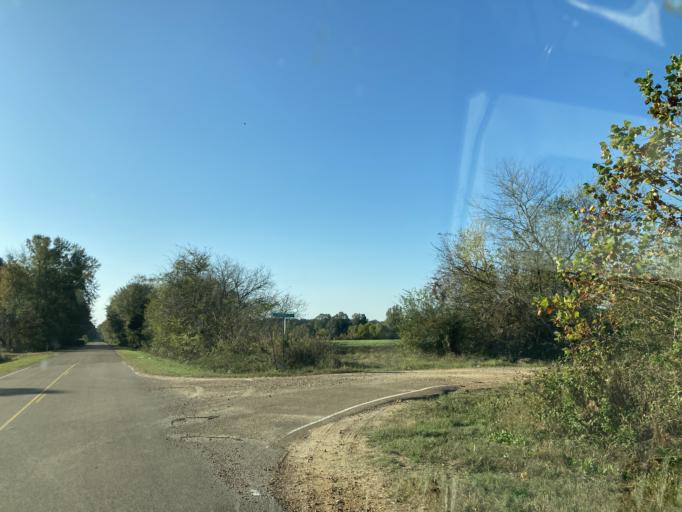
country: US
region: Mississippi
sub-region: Madison County
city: Canton
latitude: 32.7276
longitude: -90.1667
